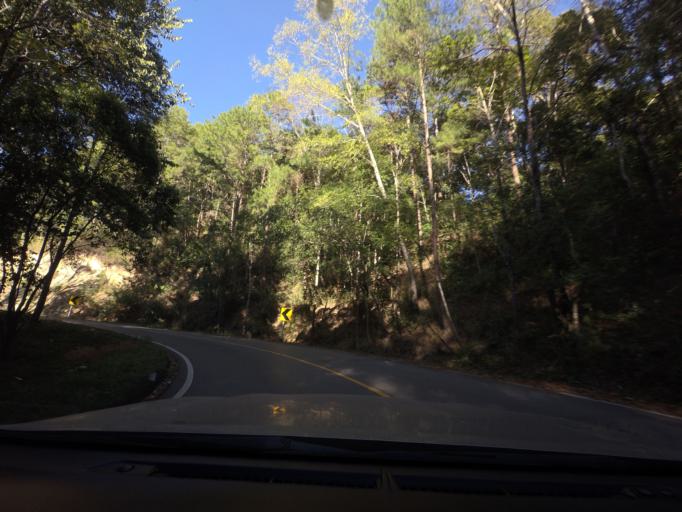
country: TH
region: Mae Hong Son
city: Mae Hi
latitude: 19.2526
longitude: 98.6387
